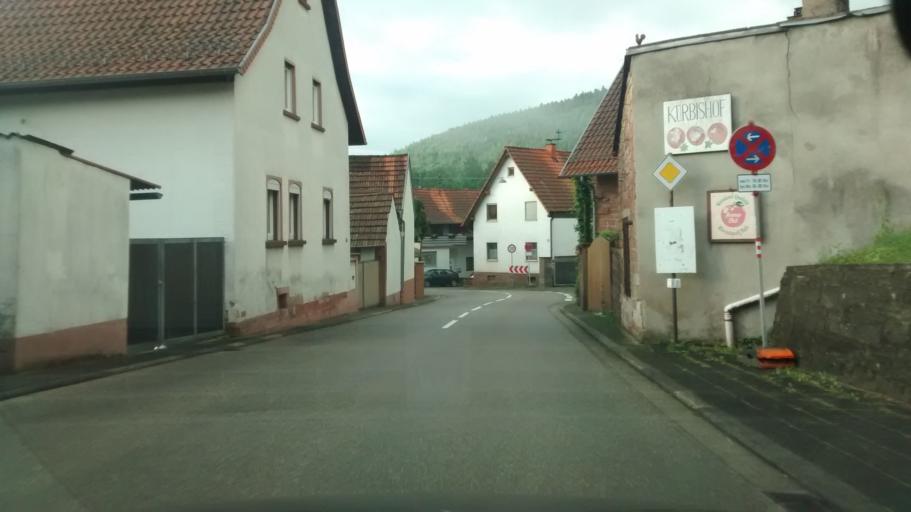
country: DE
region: Rheinland-Pfalz
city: Birkenhordt
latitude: 49.1154
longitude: 7.9292
